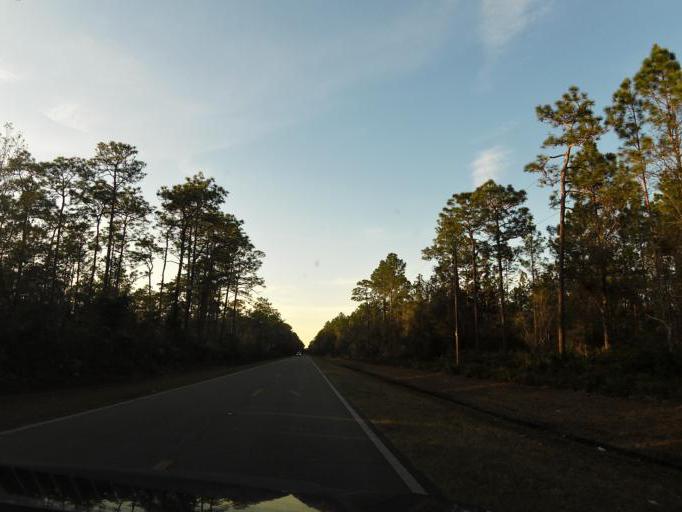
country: US
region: Florida
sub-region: Clay County
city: Green Cove Springs
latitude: 29.8782
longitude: -81.5545
